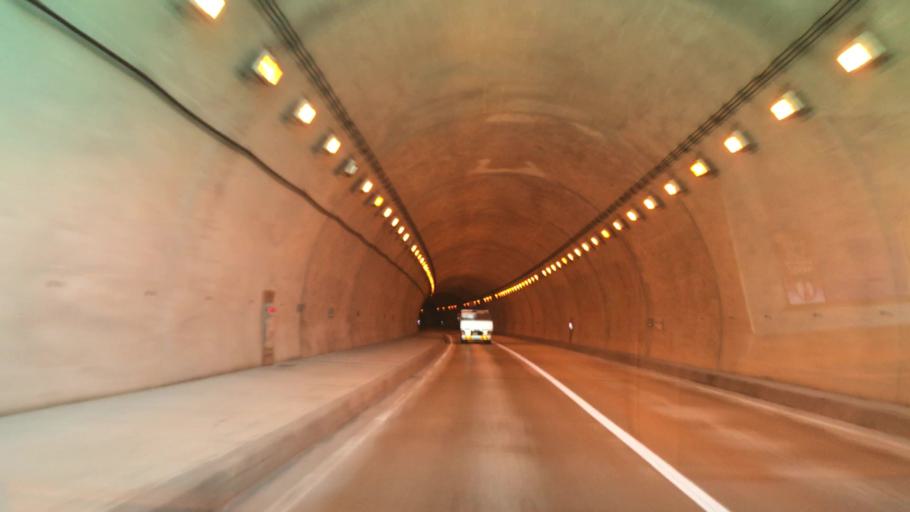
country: JP
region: Hokkaido
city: Iwanai
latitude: 43.0891
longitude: 140.4658
